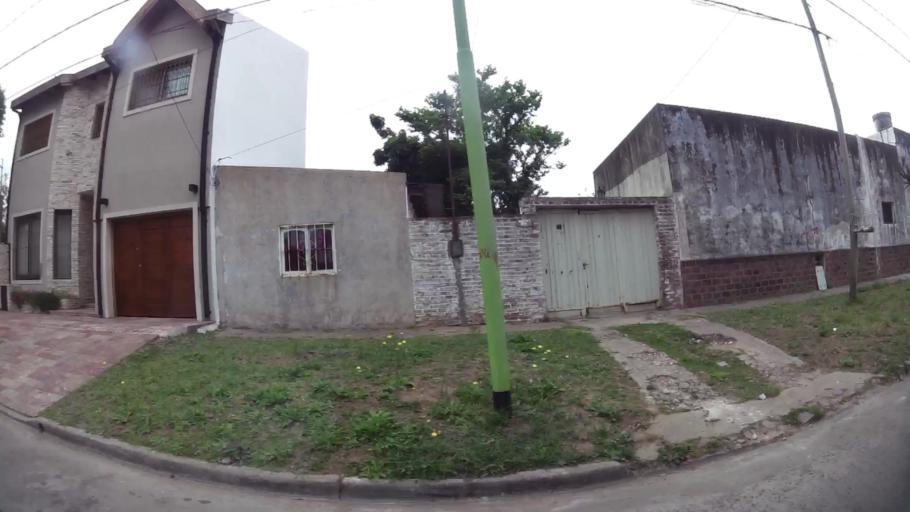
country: AR
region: Buenos Aires
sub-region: Partido de Campana
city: Campana
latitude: -34.1723
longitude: -58.9578
